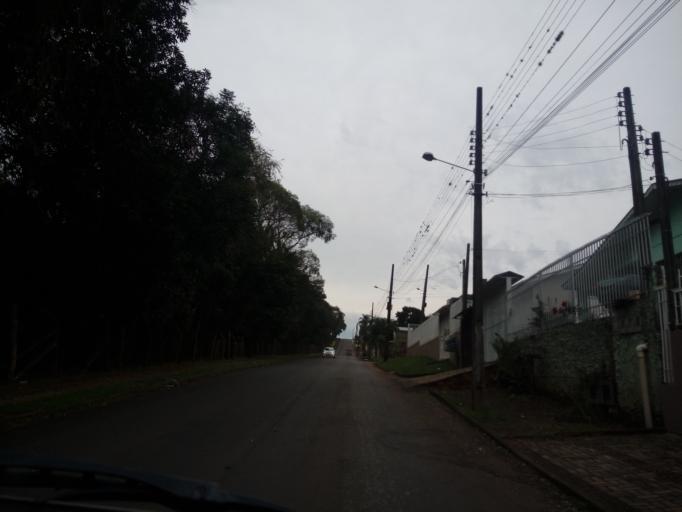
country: BR
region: Santa Catarina
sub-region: Chapeco
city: Chapeco
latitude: -27.0745
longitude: -52.6170
